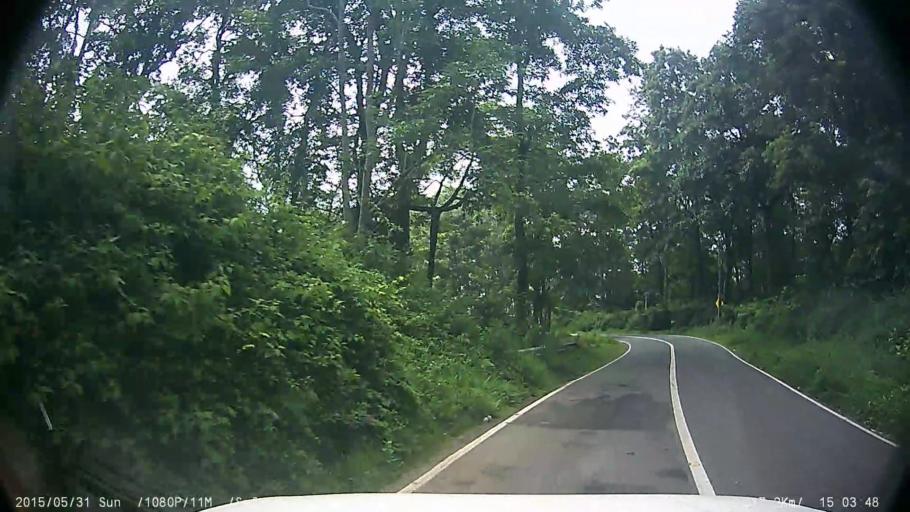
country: IN
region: Kerala
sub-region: Wayanad
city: Kalpetta
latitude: 11.6336
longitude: 76.2148
